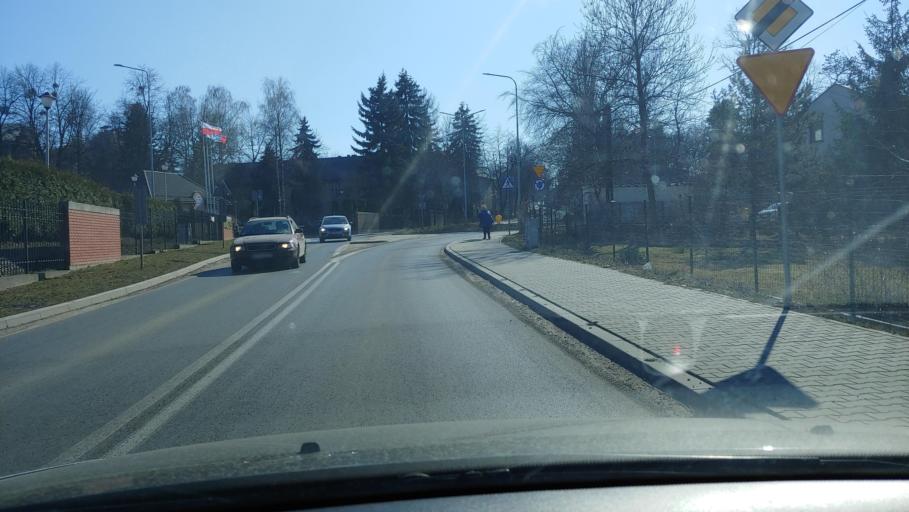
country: PL
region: Lesser Poland Voivodeship
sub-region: Powiat chrzanowski
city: Trzebinia
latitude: 50.1783
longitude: 19.4544
